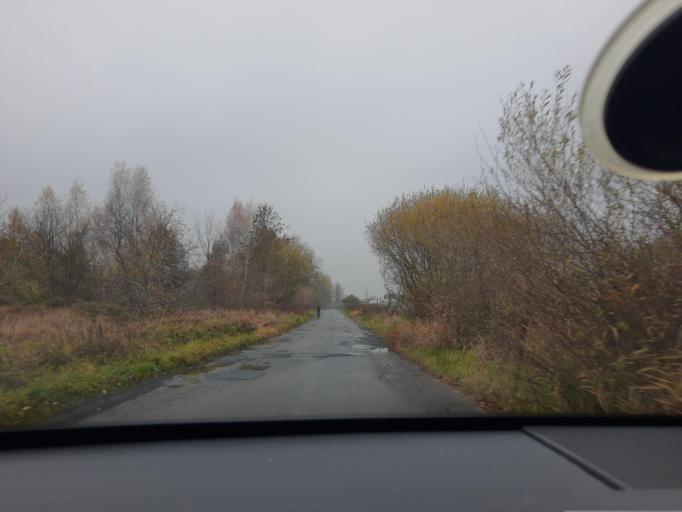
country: PL
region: Lodz Voivodeship
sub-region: Powiat pabianicki
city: Konstantynow Lodzki
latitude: 51.7474
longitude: 19.3716
